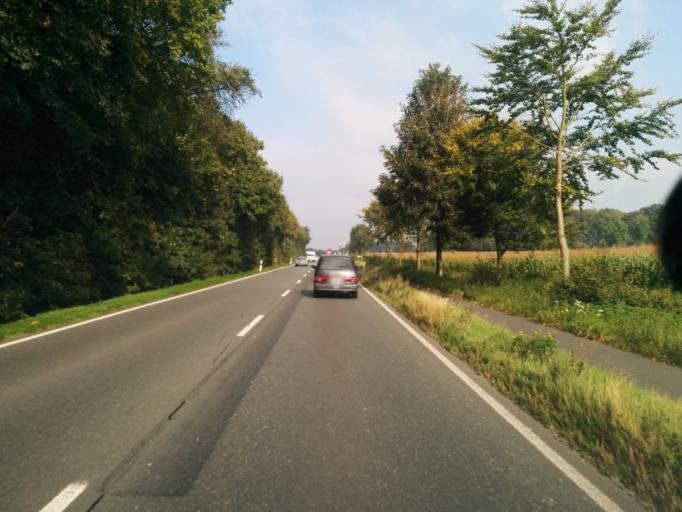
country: DE
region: North Rhine-Westphalia
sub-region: Regierungsbezirk Munster
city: Dulmen
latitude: 51.8481
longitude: 7.2522
